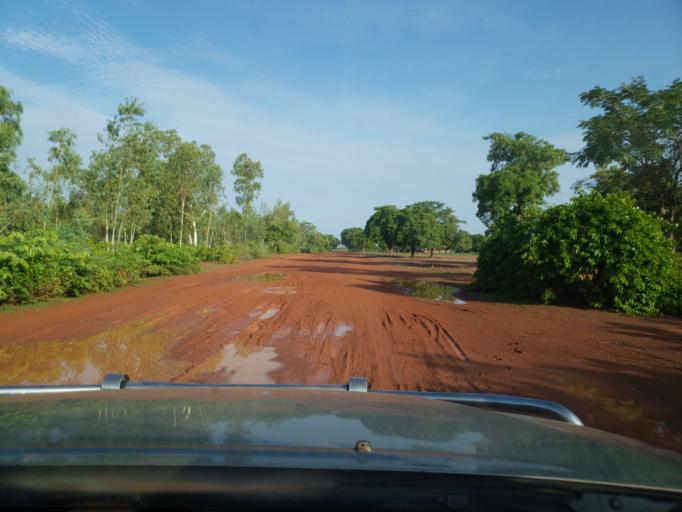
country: ML
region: Sikasso
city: Koutiala
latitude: 12.4269
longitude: -5.5993
